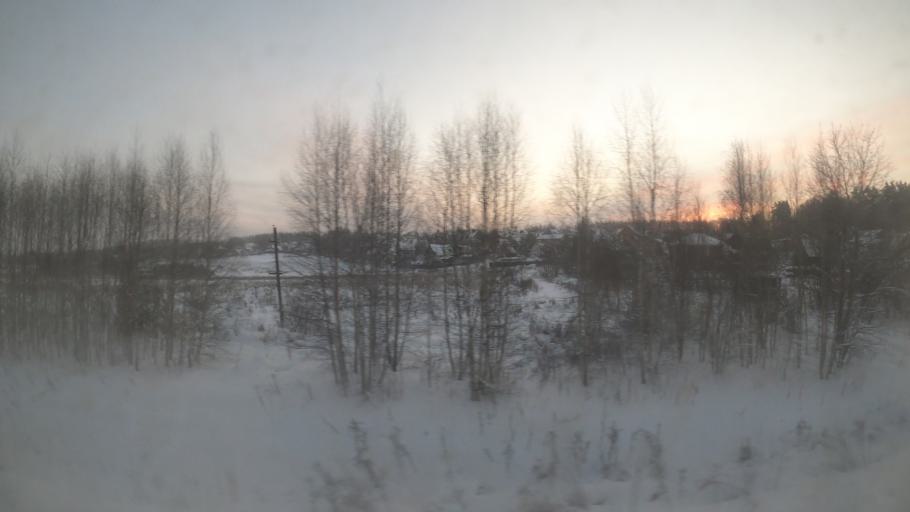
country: RU
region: Moskovskaya
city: Lugovaya
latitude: 56.0667
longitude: 37.4935
